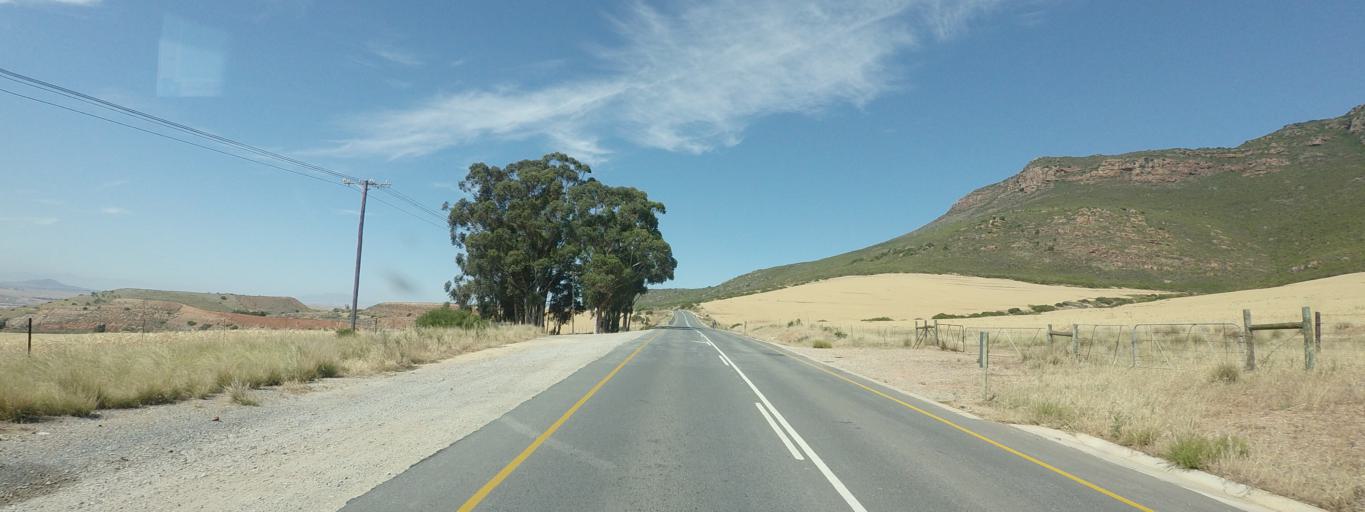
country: ZA
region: Western Cape
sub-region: West Coast District Municipality
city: Piketberg
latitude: -32.9212
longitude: 18.7580
